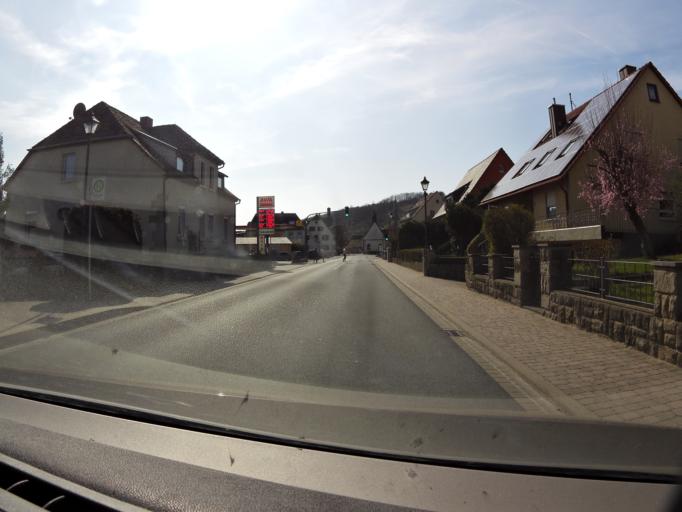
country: DE
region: Bavaria
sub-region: Regierungsbezirk Unterfranken
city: Rottingen
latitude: 49.5113
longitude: 9.9729
